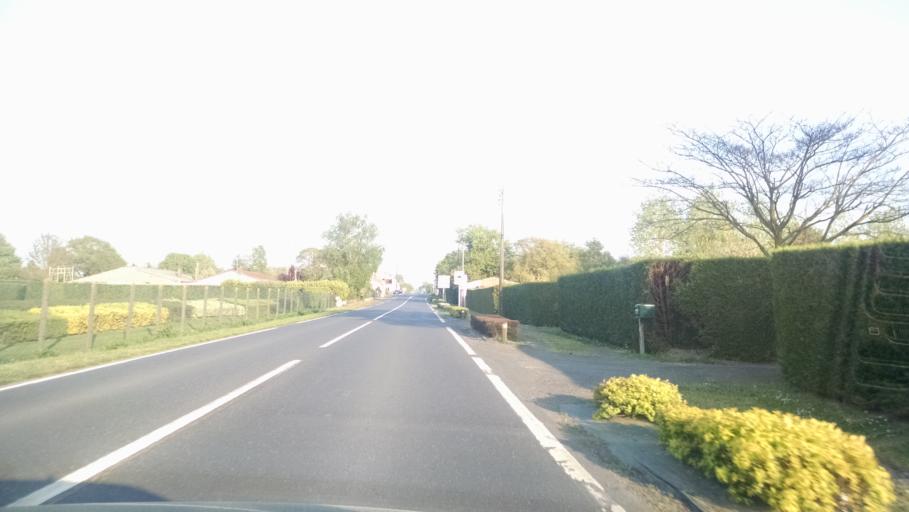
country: FR
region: Pays de la Loire
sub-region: Departement de la Loire-Atlantique
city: Boussay
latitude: 47.0597
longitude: -1.1844
